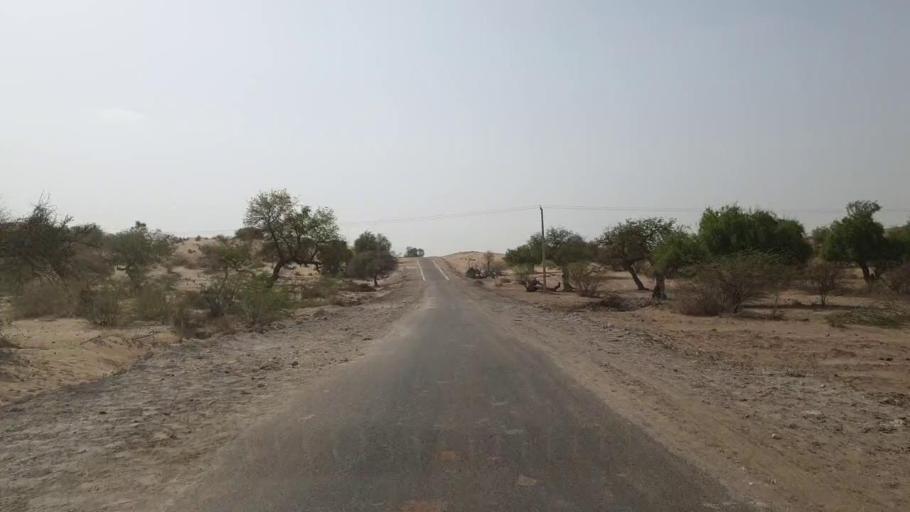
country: PK
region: Sindh
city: Mithi
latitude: 24.6186
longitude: 69.9176
